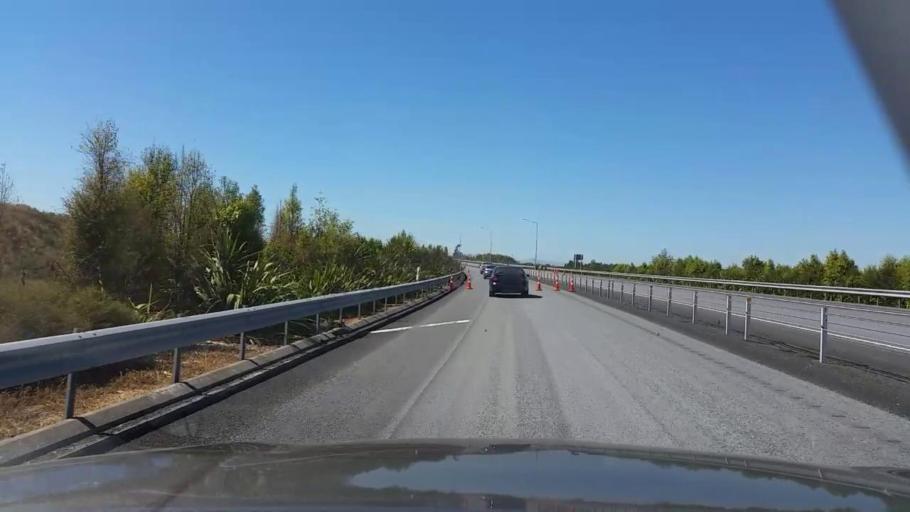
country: NZ
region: Waikato
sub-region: Hamilton City
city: Hamilton
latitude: -37.7511
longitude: 175.2189
